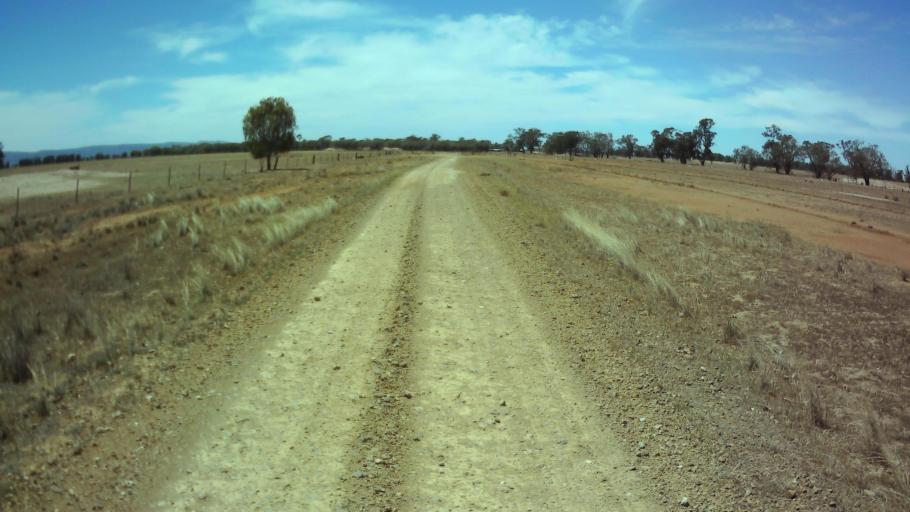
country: AU
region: New South Wales
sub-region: Weddin
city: Grenfell
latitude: -33.8647
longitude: 147.7618
